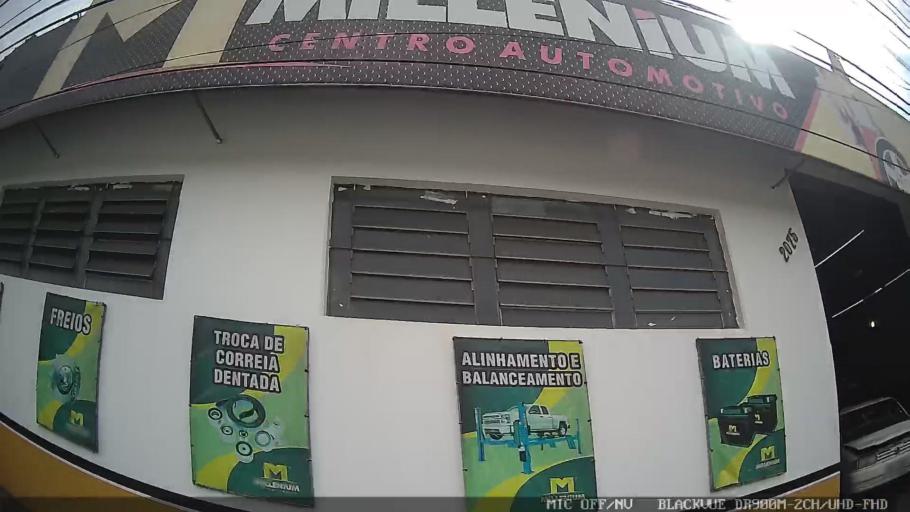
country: BR
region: Sao Paulo
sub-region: Salto
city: Salto
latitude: -23.1919
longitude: -47.2832
